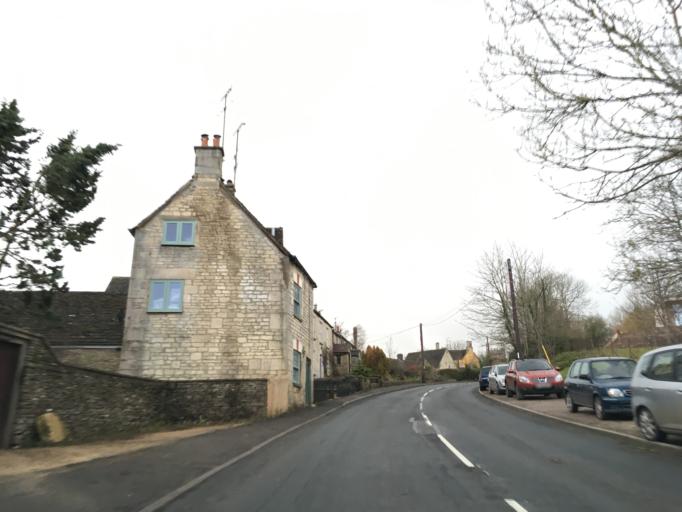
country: GB
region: England
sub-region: Gloucestershire
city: Nailsworth
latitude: 51.6815
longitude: -2.2318
